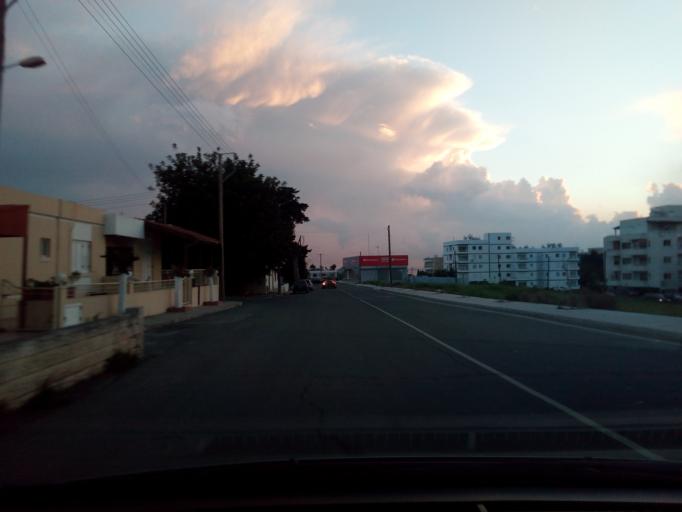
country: CY
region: Pafos
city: Paphos
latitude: 34.7732
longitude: 32.4349
